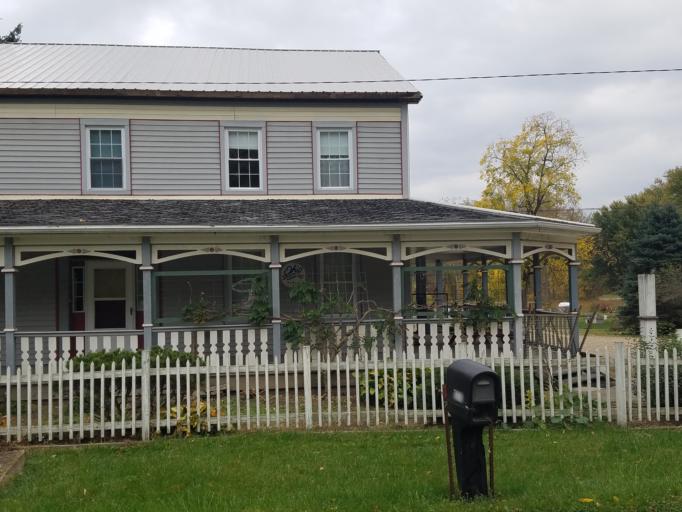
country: US
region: Ohio
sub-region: Richland County
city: Mansfield
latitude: 40.6899
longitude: -82.5114
